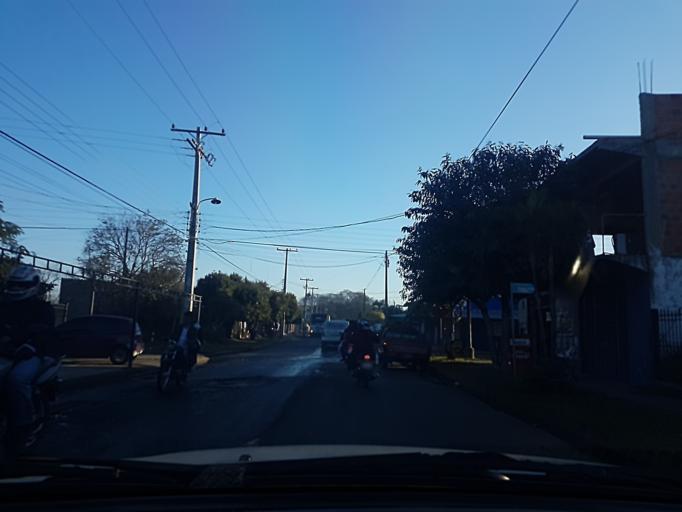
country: PY
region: Central
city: Colonia Mariano Roque Alonso
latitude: -25.2207
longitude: -57.5233
